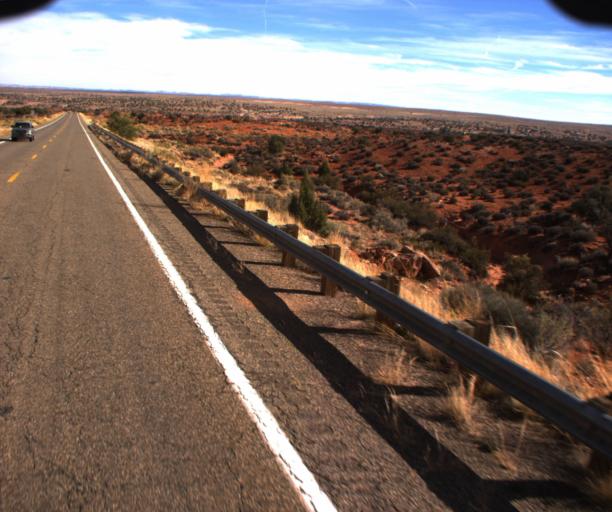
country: US
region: Arizona
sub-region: Coconino County
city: Kaibito
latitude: 36.5996
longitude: -111.0920
